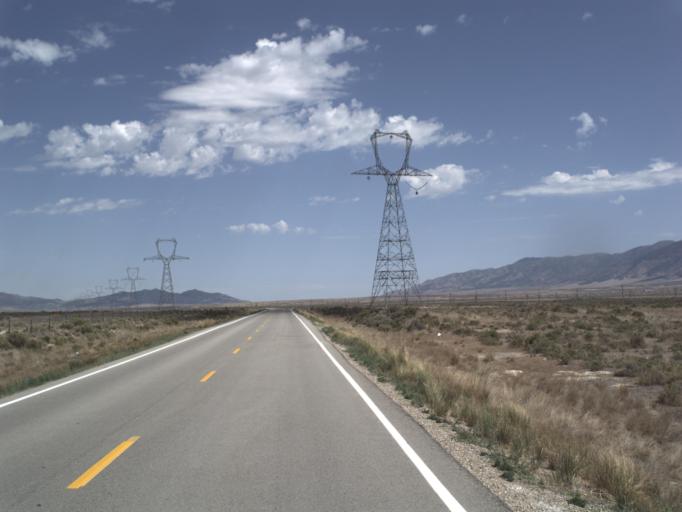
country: US
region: Utah
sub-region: Tooele County
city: Tooele
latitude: 40.2591
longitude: -112.3982
